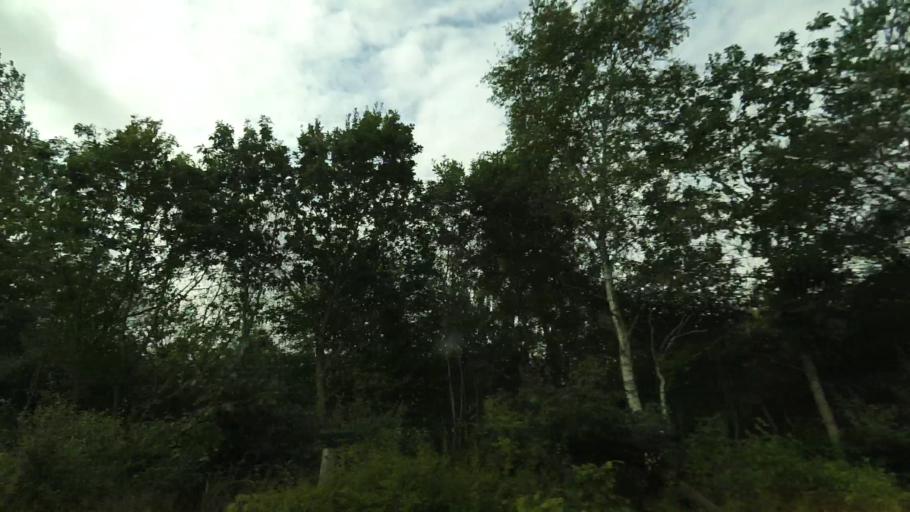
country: DK
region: Central Jutland
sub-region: Syddjurs Kommune
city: Ryomgard
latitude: 56.3681
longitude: 10.5024
